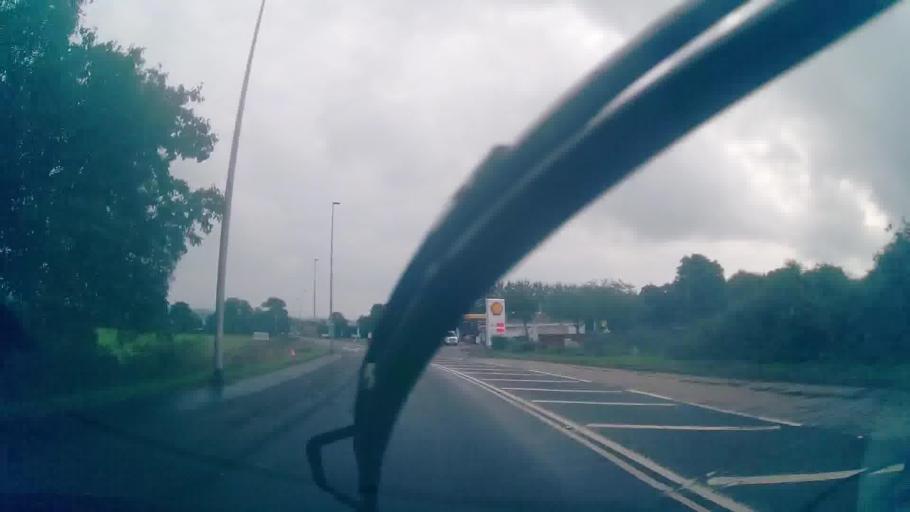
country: GB
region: Scotland
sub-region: Dumfries and Galloway
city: Locharbriggs
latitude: 55.0689
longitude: -3.5559
